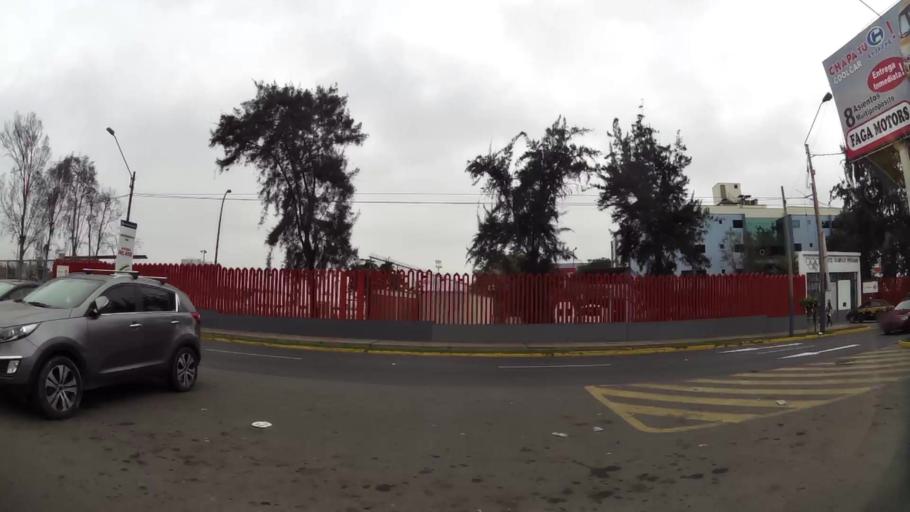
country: PE
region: Lima
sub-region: Lima
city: San Luis
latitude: -12.0793
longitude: -77.0007
